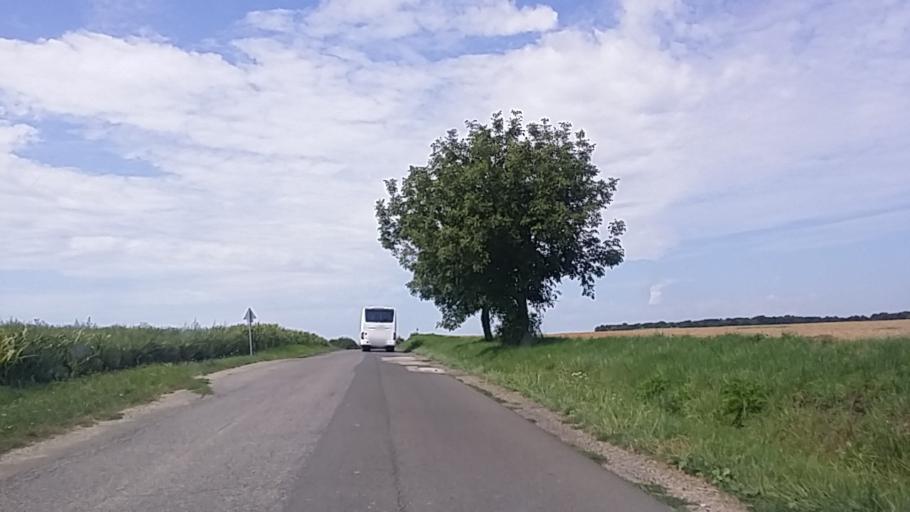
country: HU
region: Tolna
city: Dombovar
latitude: 46.3328
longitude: 18.1138
